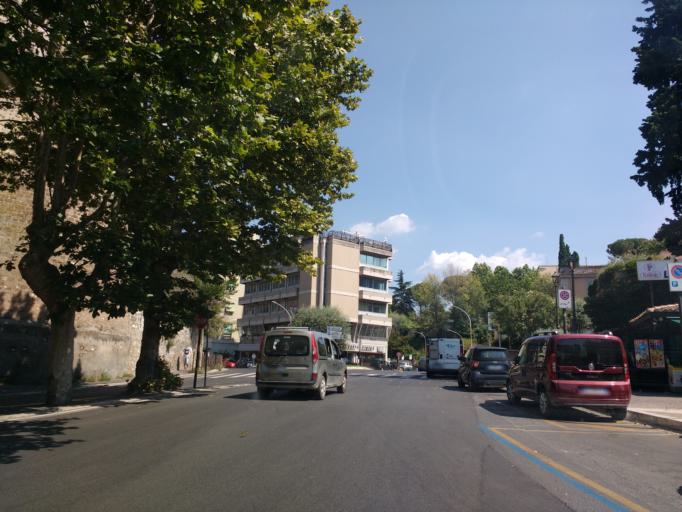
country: IT
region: Latium
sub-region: Citta metropolitana di Roma Capitale
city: Tivoli
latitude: 41.9599
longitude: 12.7977
